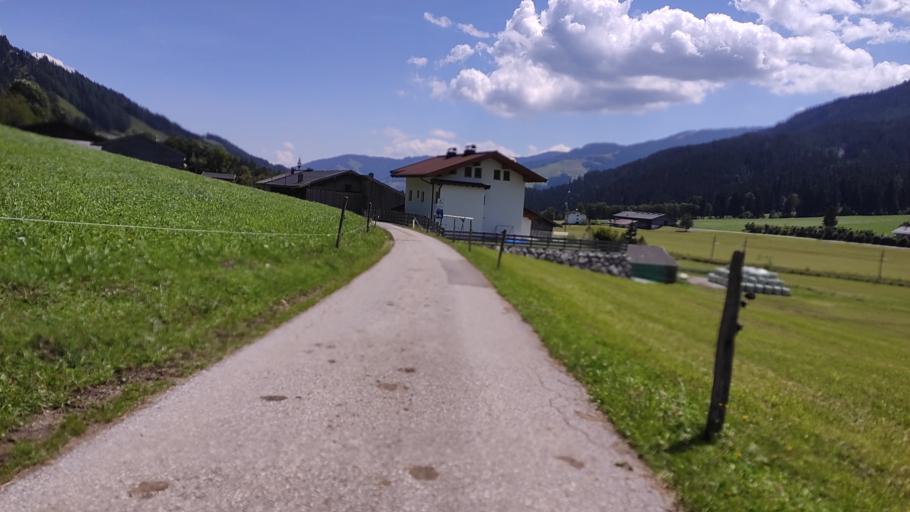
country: AT
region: Tyrol
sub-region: Politischer Bezirk Kitzbuhel
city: Hochfilzen
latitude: 47.4564
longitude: 12.6658
